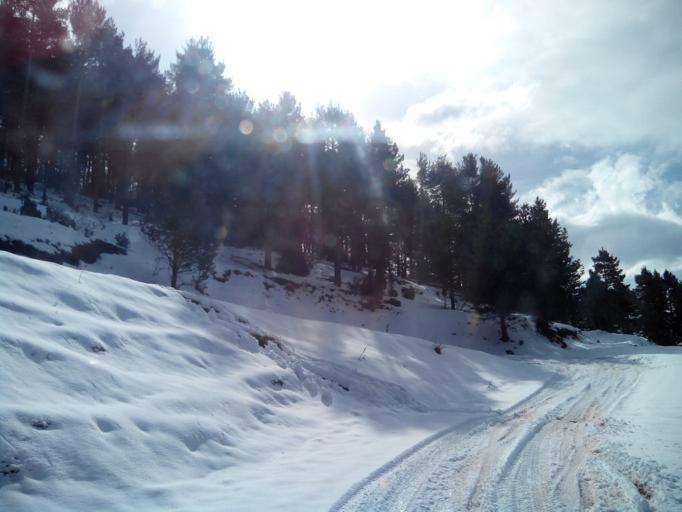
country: ES
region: Catalonia
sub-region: Provincia de Barcelona
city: Sant Julia de Cerdanyola
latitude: 42.1930
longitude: 1.9276
